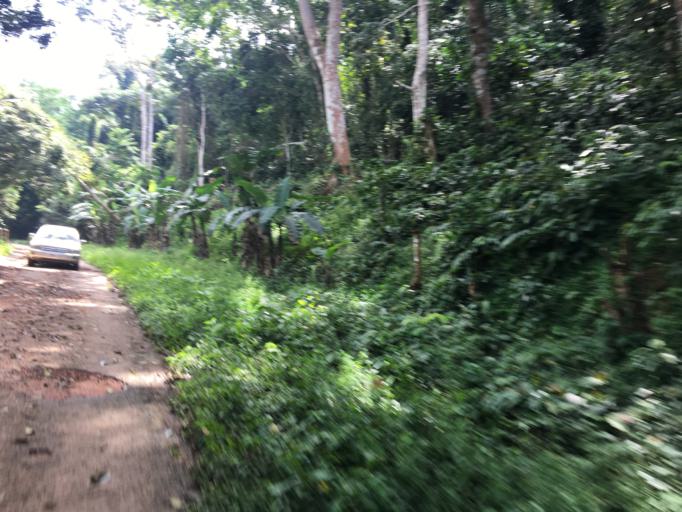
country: TG
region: Plateaux
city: Kpalime
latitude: 6.9539
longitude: 0.5828
